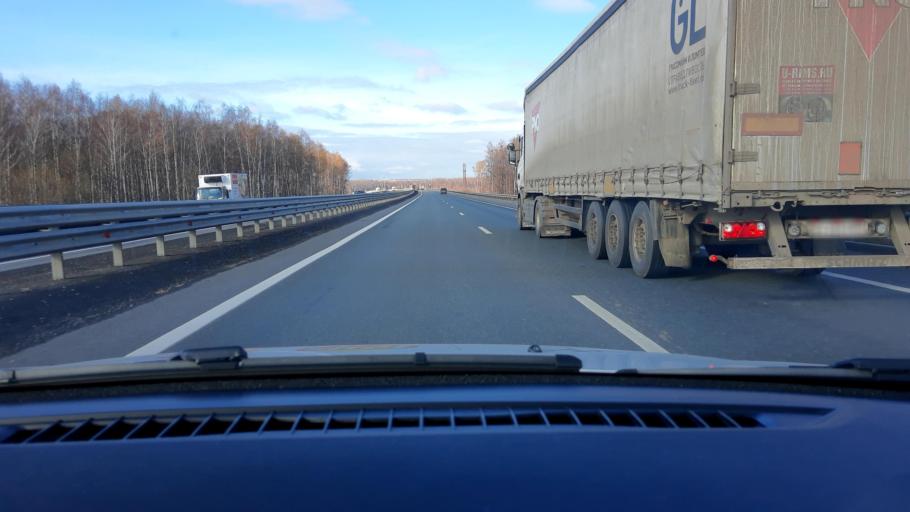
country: RU
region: Nizjnij Novgorod
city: Burevestnik
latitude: 56.1185
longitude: 43.8171
